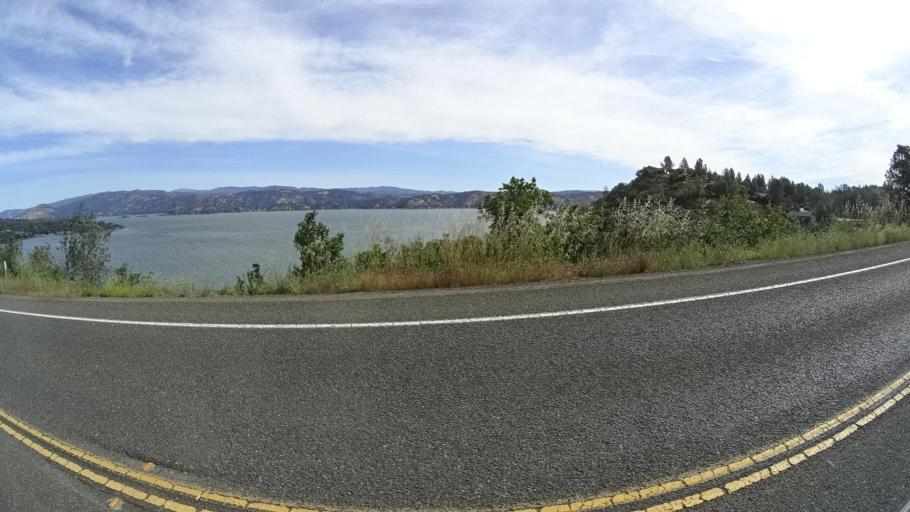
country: US
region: California
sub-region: Lake County
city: Soda Bay
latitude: 38.9602
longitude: -122.7296
